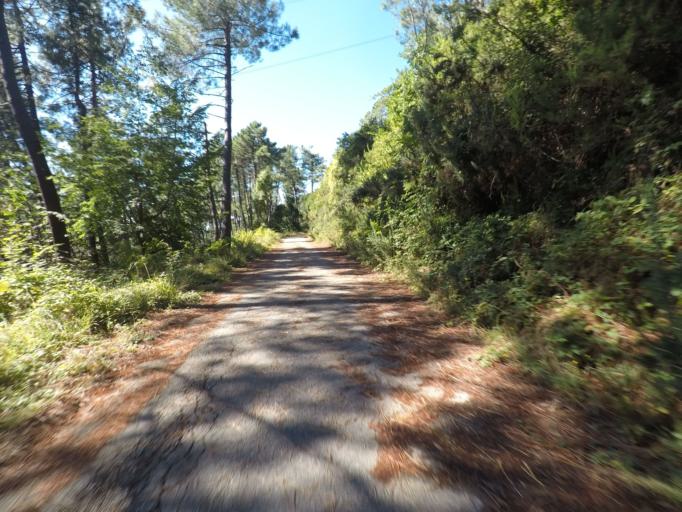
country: IT
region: Tuscany
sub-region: Provincia di Massa-Carrara
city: Montignoso
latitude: 44.0325
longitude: 10.1679
